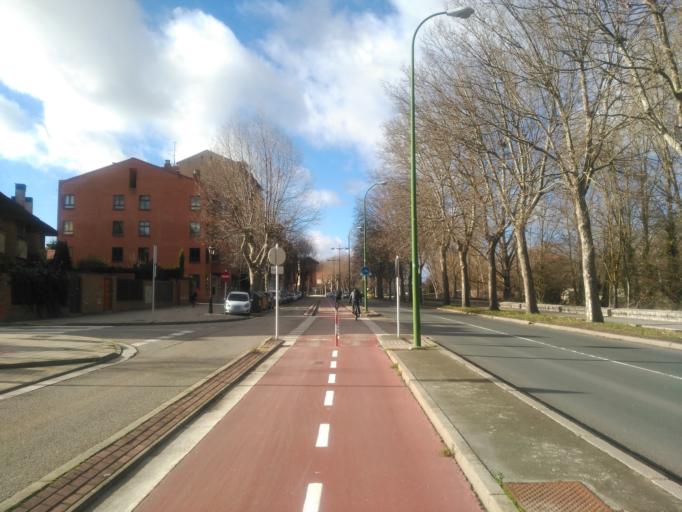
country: ES
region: Castille and Leon
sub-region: Provincia de Burgos
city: Burgos
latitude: 42.3393
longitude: -3.7153
